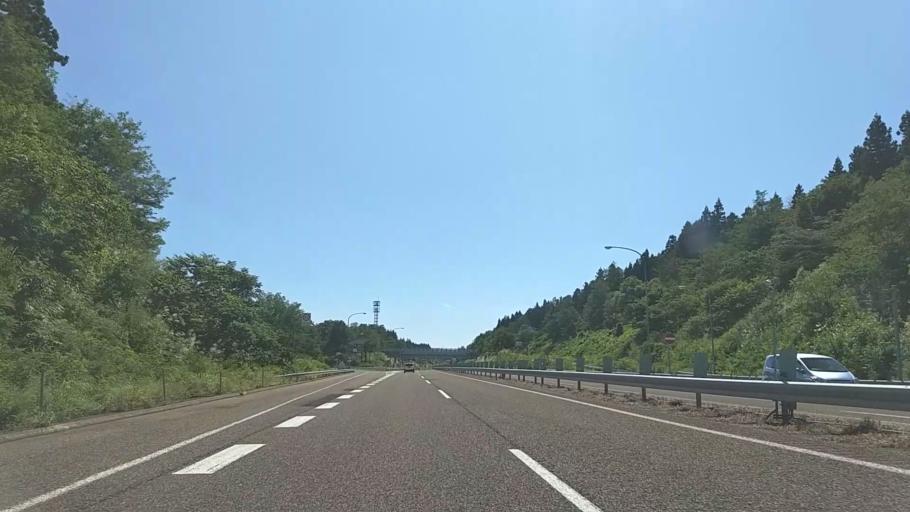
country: JP
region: Niigata
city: Arai
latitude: 36.9720
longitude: 138.2216
